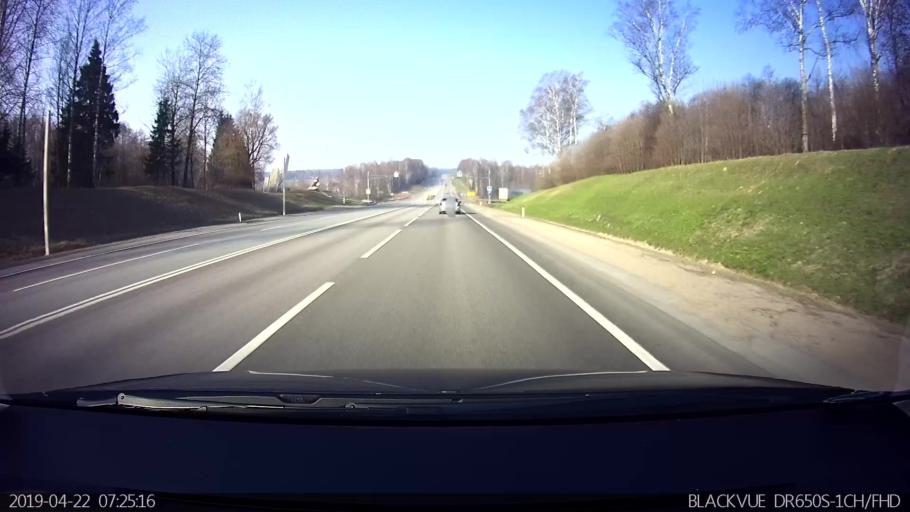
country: RU
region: Smolensk
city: Vyaz'ma
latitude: 55.1942
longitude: 34.0946
